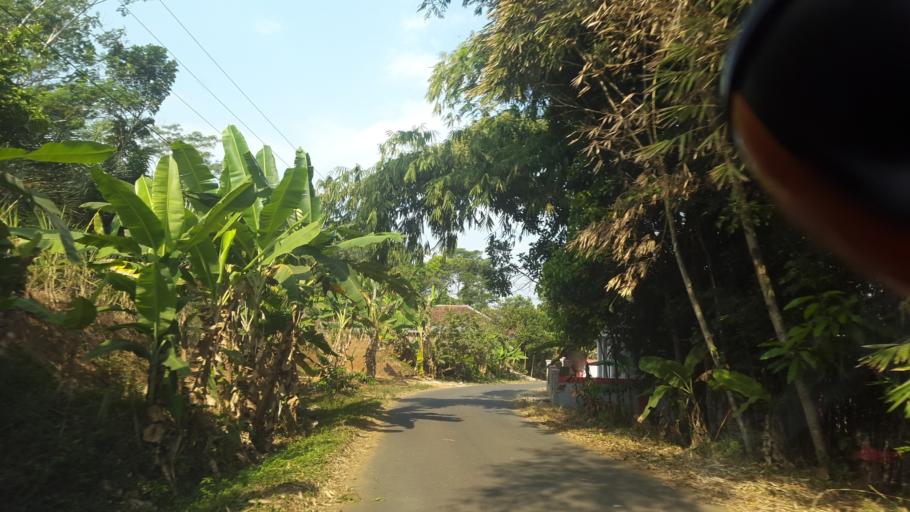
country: ID
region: West Java
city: Gelarpadang
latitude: -7.2463
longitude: 106.9332
